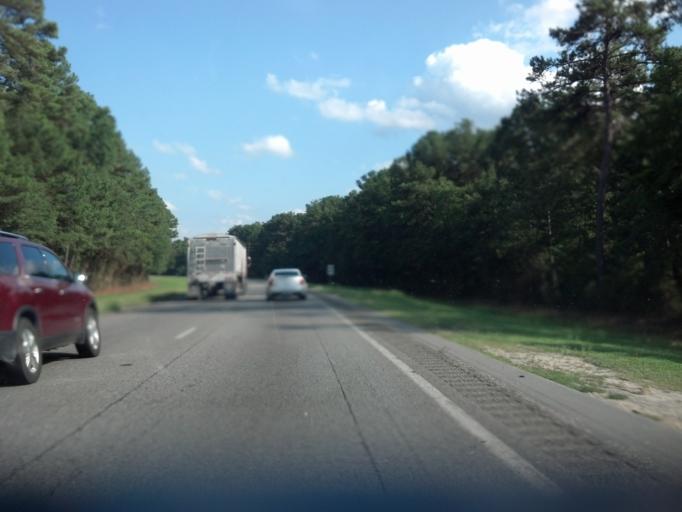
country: US
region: North Carolina
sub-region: Nash County
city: Rocky Mount
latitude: 35.9397
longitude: -77.7552
